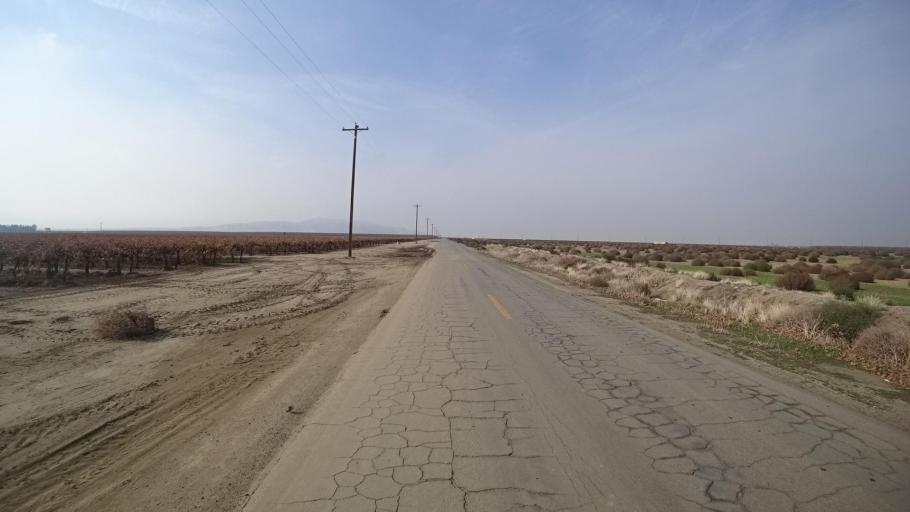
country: US
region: California
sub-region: Kern County
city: Lebec
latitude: 35.0309
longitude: -118.9193
